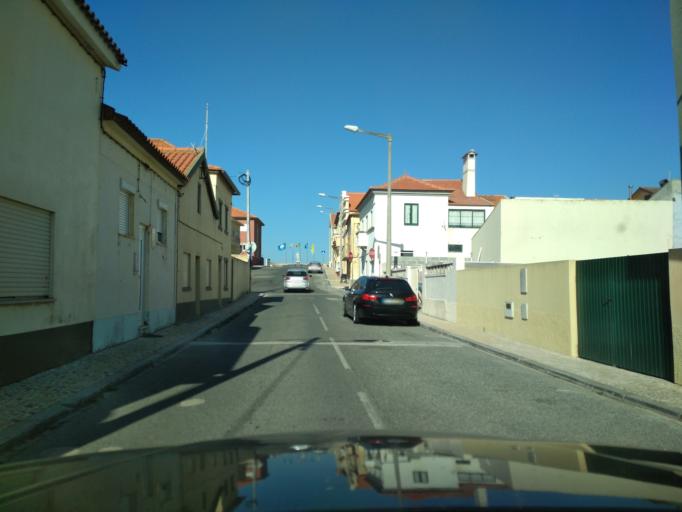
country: PT
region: Coimbra
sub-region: Figueira da Foz
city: Lavos
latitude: 40.0569
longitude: -8.8868
